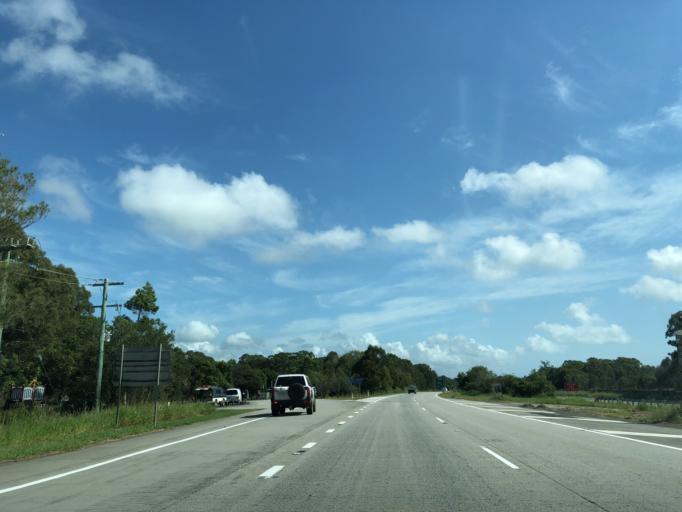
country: AU
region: New South Wales
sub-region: Byron Shire
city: Brunswick Heads
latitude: -28.5998
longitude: 153.5449
